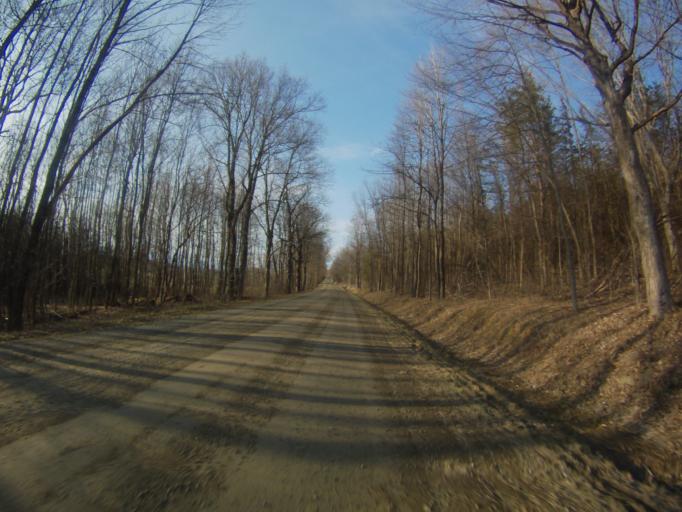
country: US
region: Vermont
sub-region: Addison County
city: Vergennes
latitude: 44.0511
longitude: -73.2919
